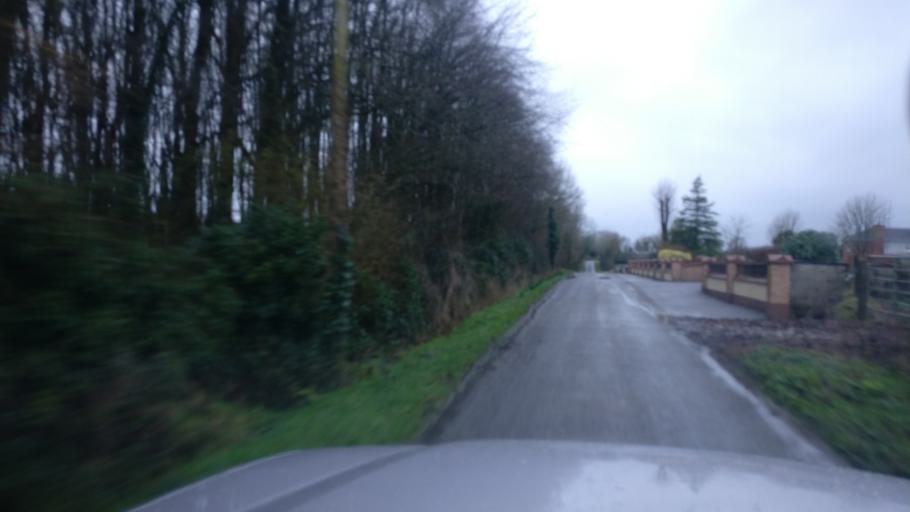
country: IE
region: Connaught
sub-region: County Galway
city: Ballinasloe
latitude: 53.2632
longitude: -8.3675
